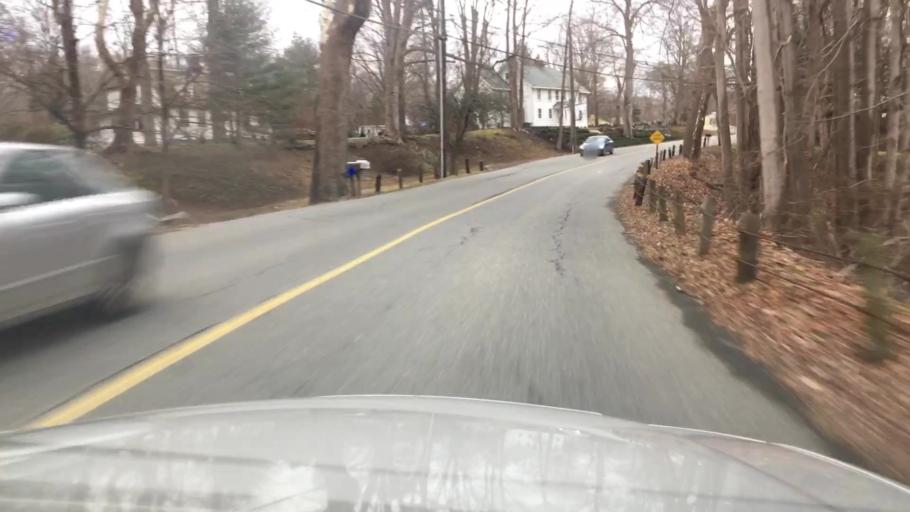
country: US
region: Connecticut
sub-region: Middlesex County
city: Essex Village
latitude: 41.3640
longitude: -72.4007
